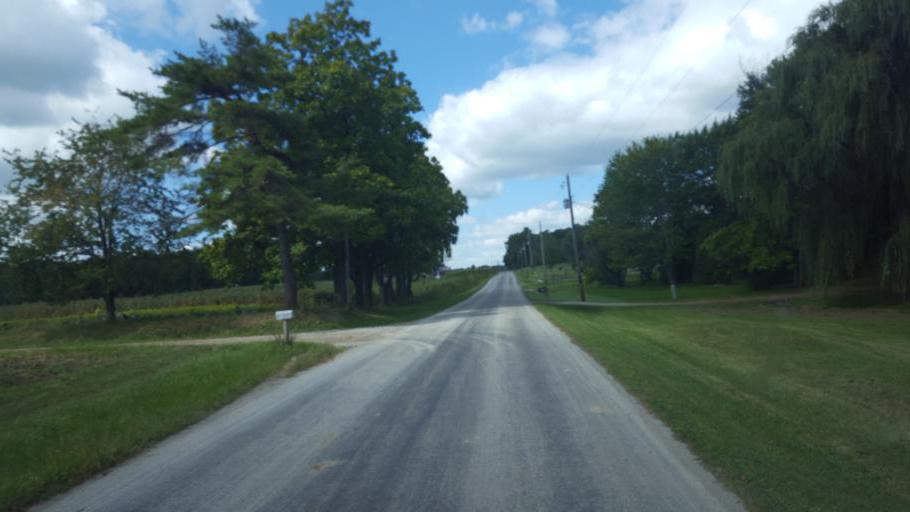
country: US
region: Ohio
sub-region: Wayne County
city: West Salem
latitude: 41.0066
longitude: -82.1286
